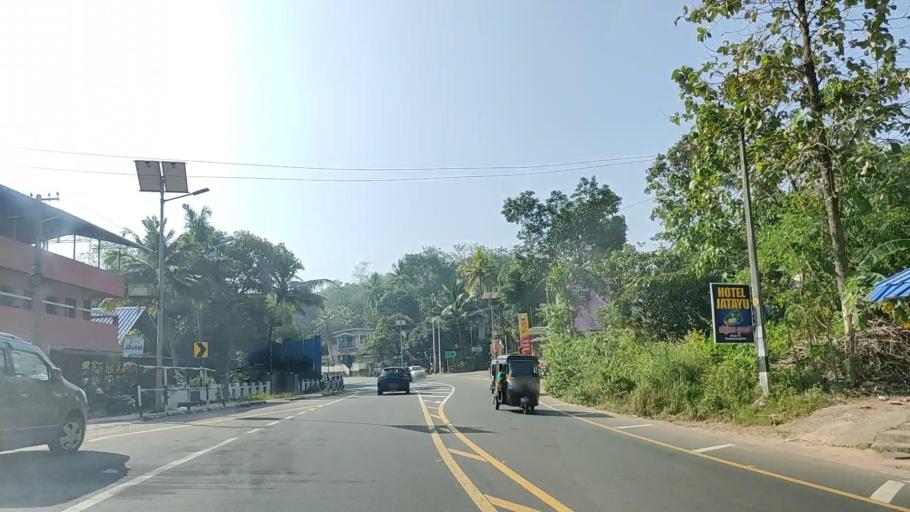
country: IN
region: Kerala
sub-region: Kollam
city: Punalur
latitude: 8.8653
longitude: 76.8708
